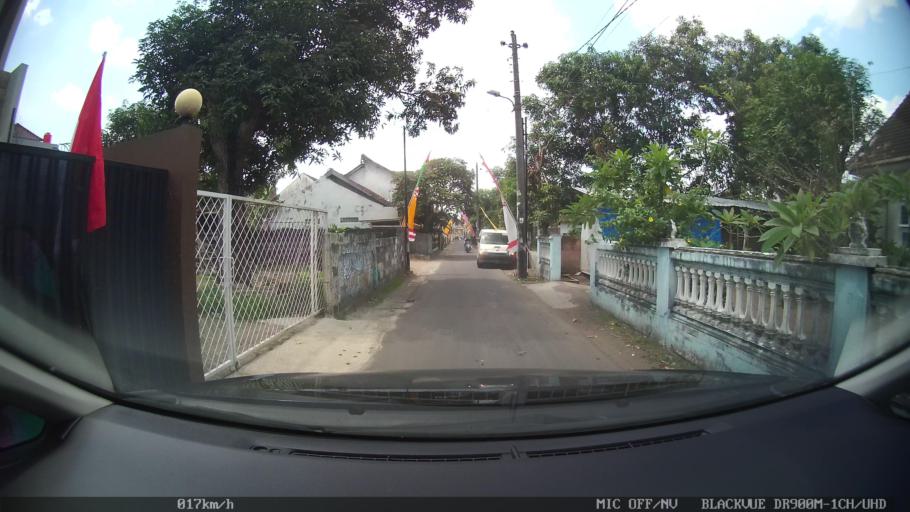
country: ID
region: Daerah Istimewa Yogyakarta
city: Yogyakarta
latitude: -7.8044
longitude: 110.3498
